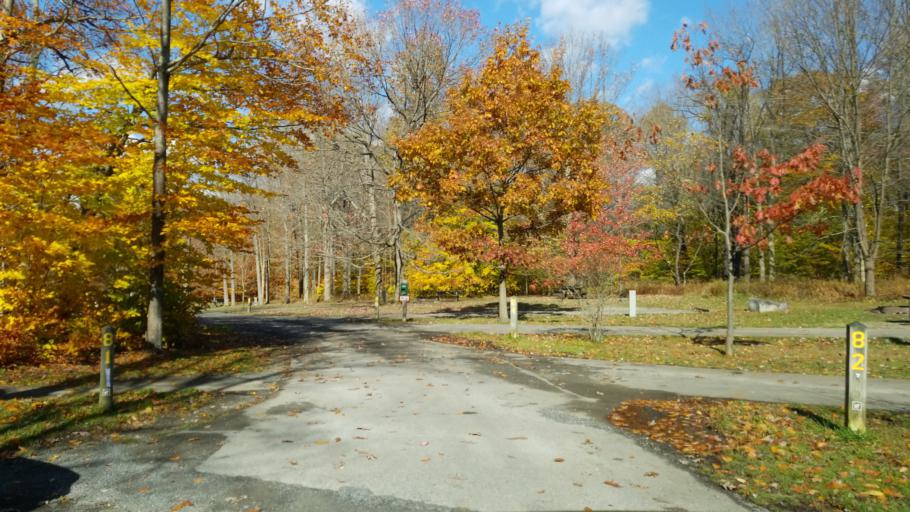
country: US
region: Pennsylvania
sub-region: Clearfield County
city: Clearfield
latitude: 41.1977
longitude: -78.5038
